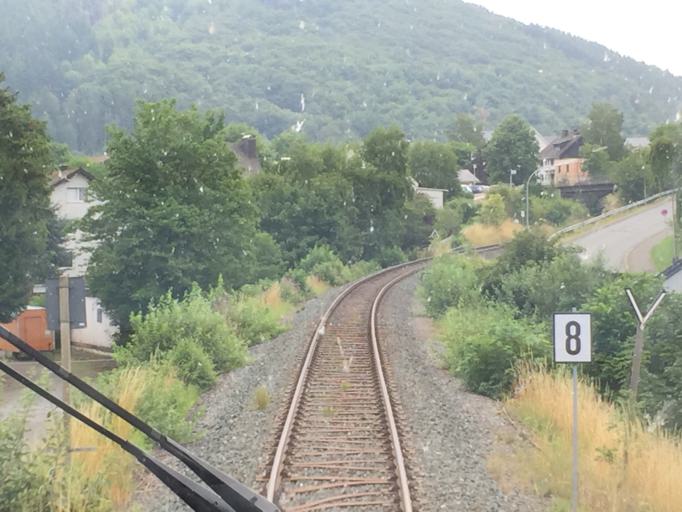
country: DE
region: Hesse
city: Willingen
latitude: 51.2929
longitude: 8.6072
